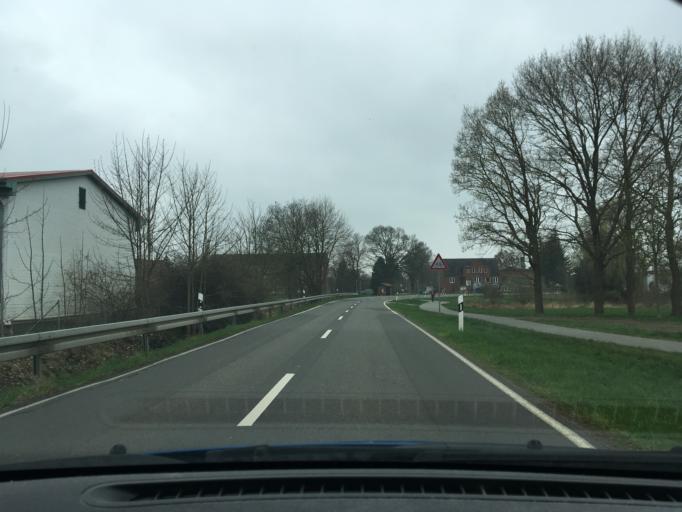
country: DE
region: Lower Saxony
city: Bleckede
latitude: 53.3295
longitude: 10.8050
